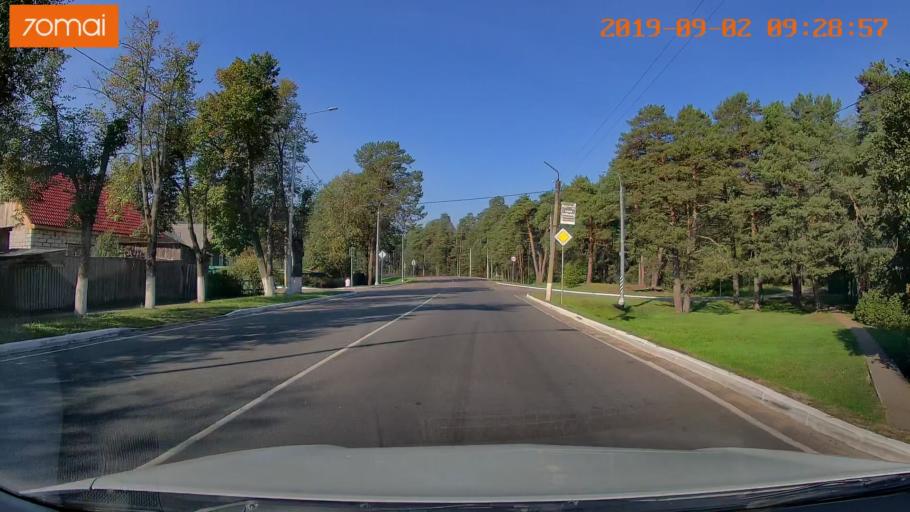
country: RU
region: Kaluga
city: Yukhnov
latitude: 54.7440
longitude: 35.2213
